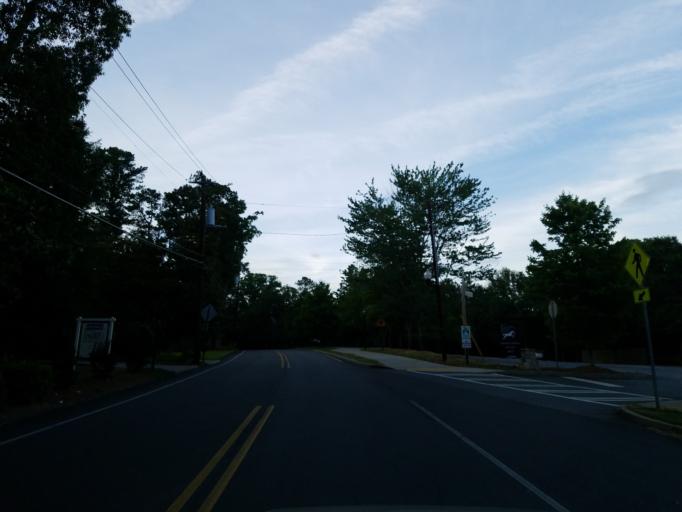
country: US
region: Georgia
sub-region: Fulton County
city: Sandy Springs
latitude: 33.8756
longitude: -84.3979
